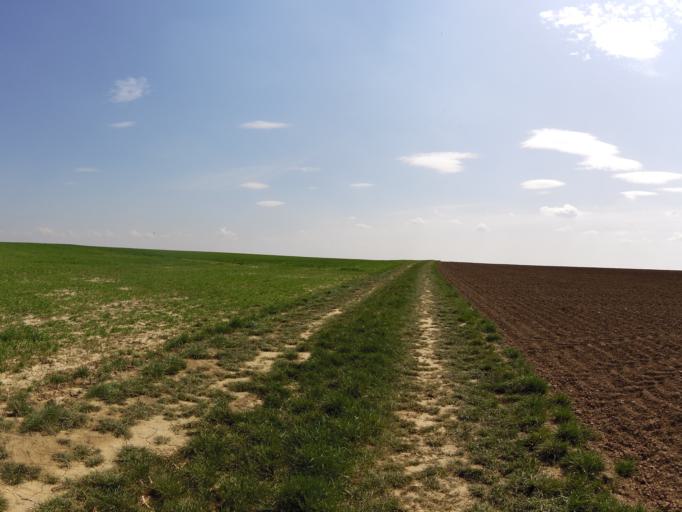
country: DE
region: Bavaria
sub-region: Regierungsbezirk Unterfranken
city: Giebelstadt
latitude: 49.6844
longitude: 9.9555
